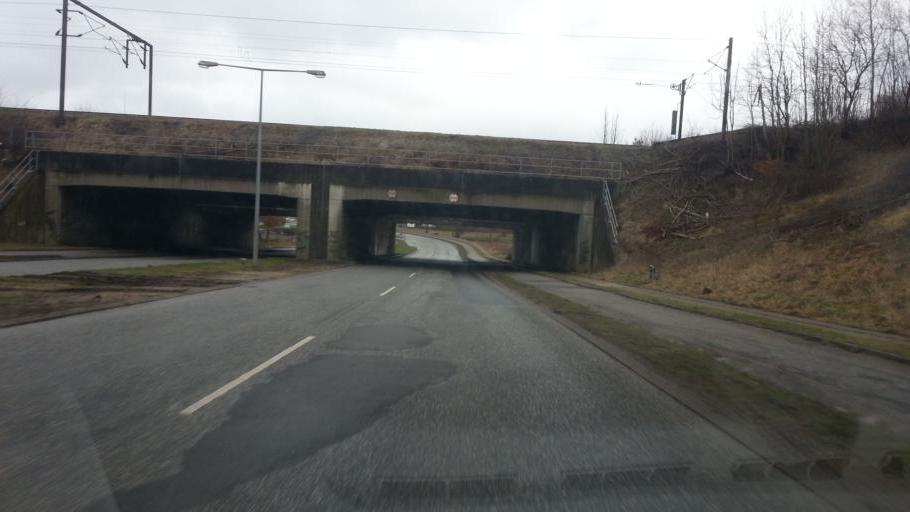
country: DK
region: South Denmark
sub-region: Fredericia Kommune
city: Fredericia
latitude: 55.5588
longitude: 9.7258
